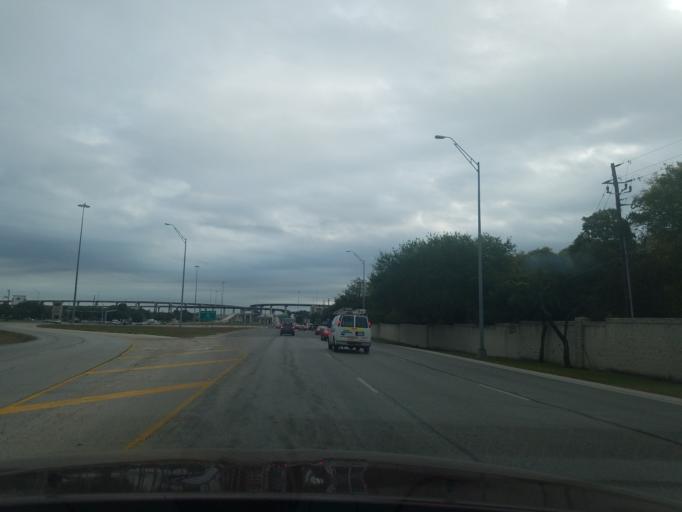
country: US
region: Texas
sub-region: Williamson County
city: Anderson Mill
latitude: 30.4652
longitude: -97.8067
